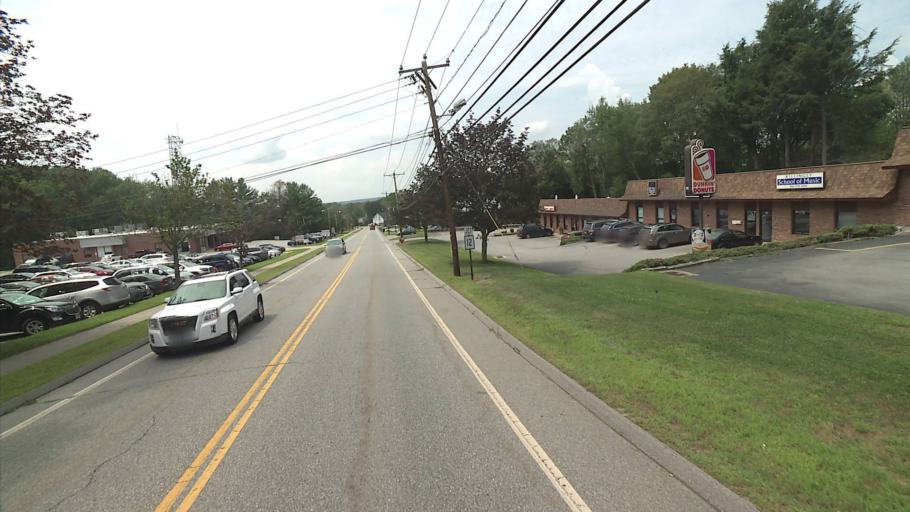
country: US
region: Connecticut
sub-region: Windham County
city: Danielson
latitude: 41.8094
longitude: -71.8743
